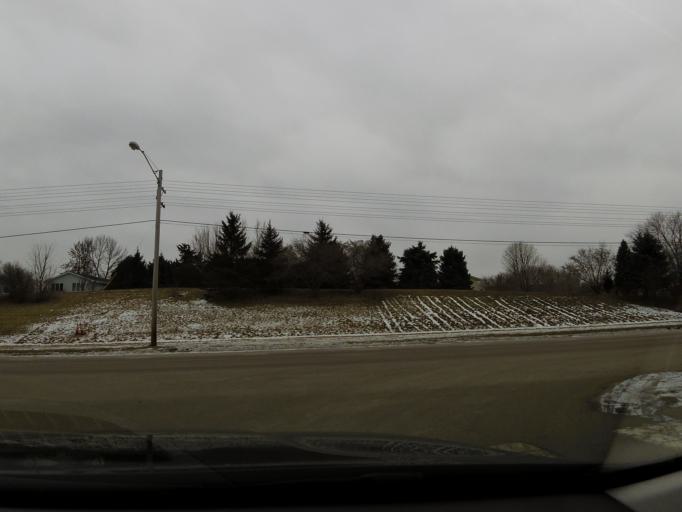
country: US
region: Minnesota
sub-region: Carver County
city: Chaska
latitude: 44.8059
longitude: -93.6148
